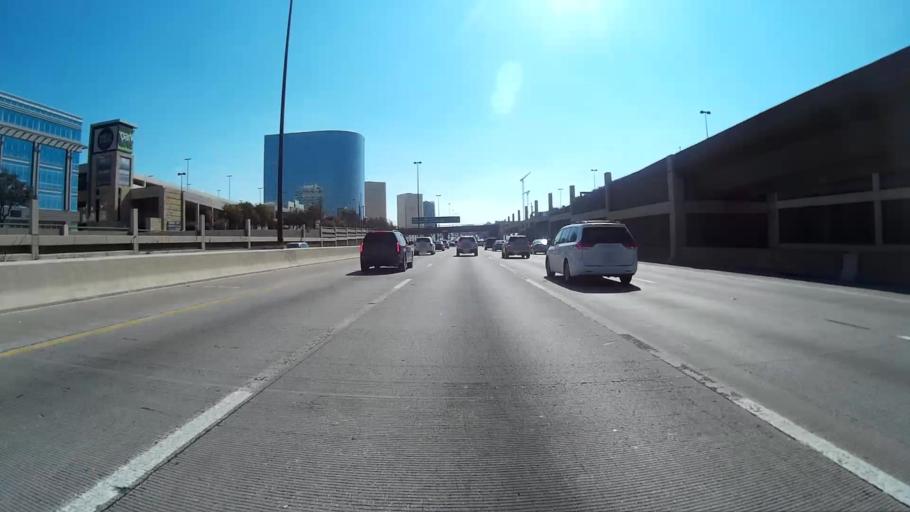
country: US
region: Texas
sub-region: Dallas County
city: University Park
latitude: 32.8704
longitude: -96.7704
